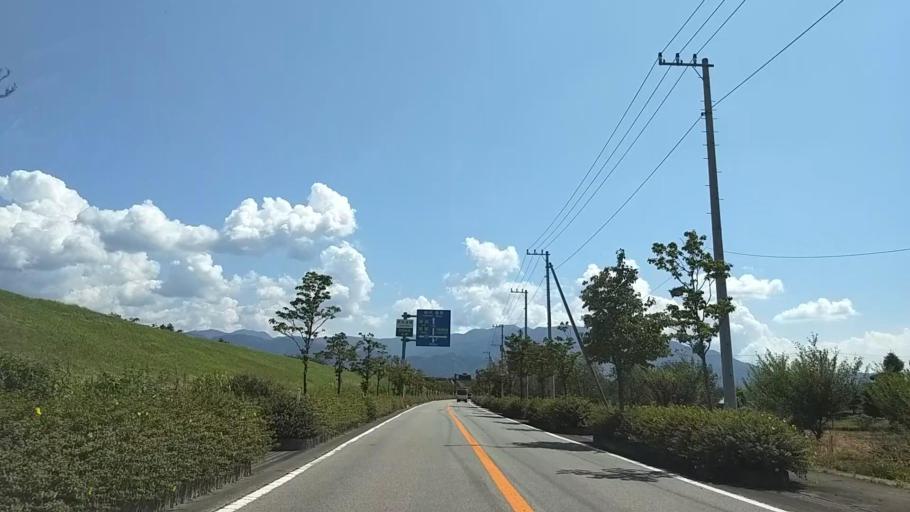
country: JP
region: Yamanashi
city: Ryuo
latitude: 35.6110
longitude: 138.5034
